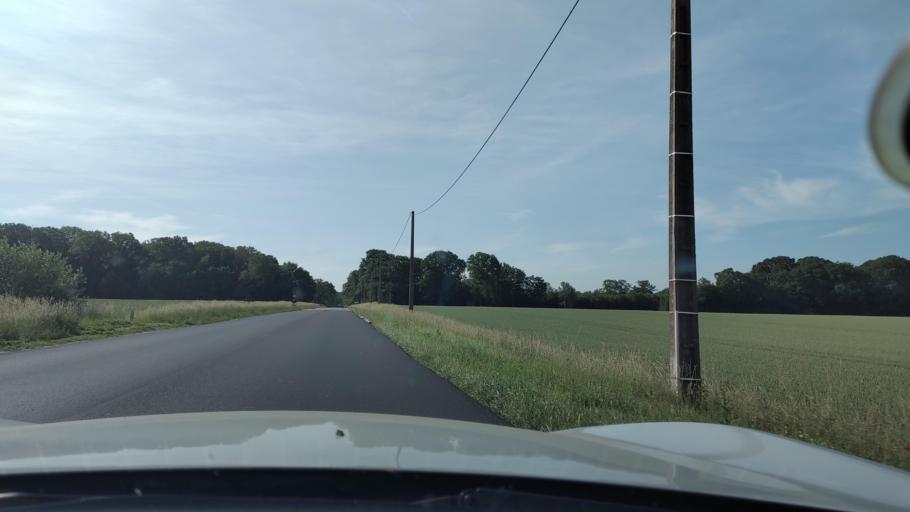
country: FR
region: Ile-de-France
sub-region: Departement de Seine-et-Marne
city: Chenoise
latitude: 48.6416
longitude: 3.1732
